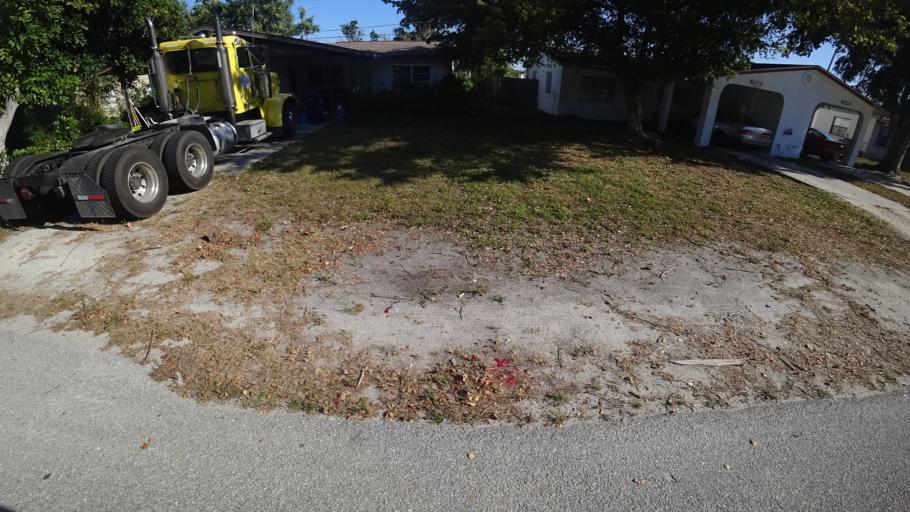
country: US
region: Florida
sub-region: Manatee County
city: Cortez
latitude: 27.4642
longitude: -82.6423
